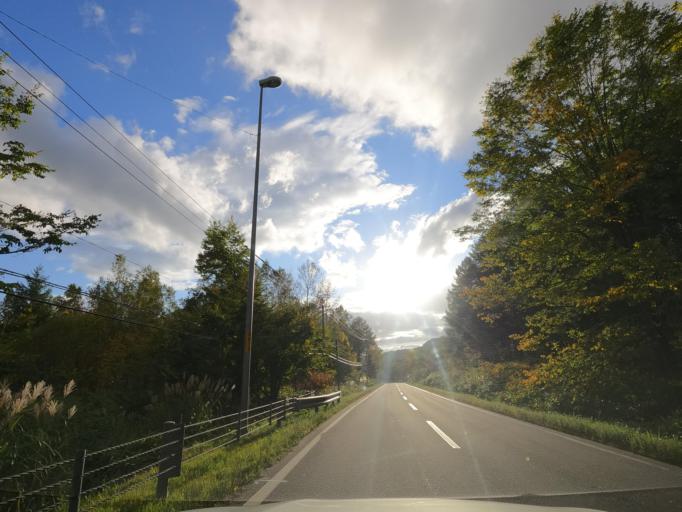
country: JP
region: Hokkaido
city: Date
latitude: 42.6538
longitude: 141.0667
